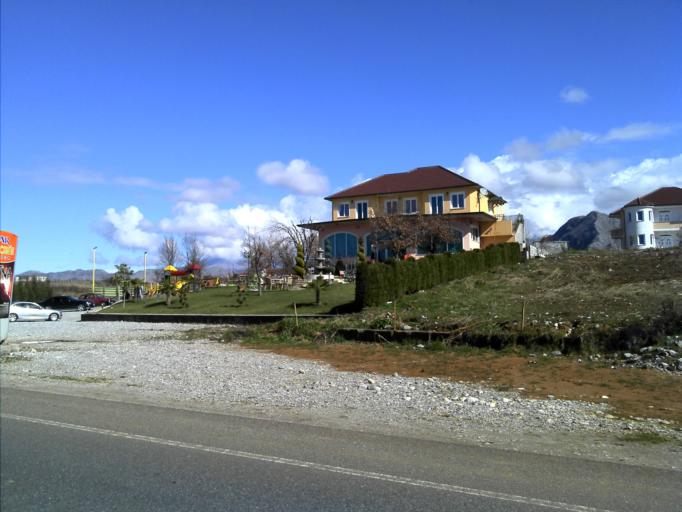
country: AL
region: Shkoder
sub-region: Rrethi i Malesia e Madhe
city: Koplik
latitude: 42.1882
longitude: 19.4575
